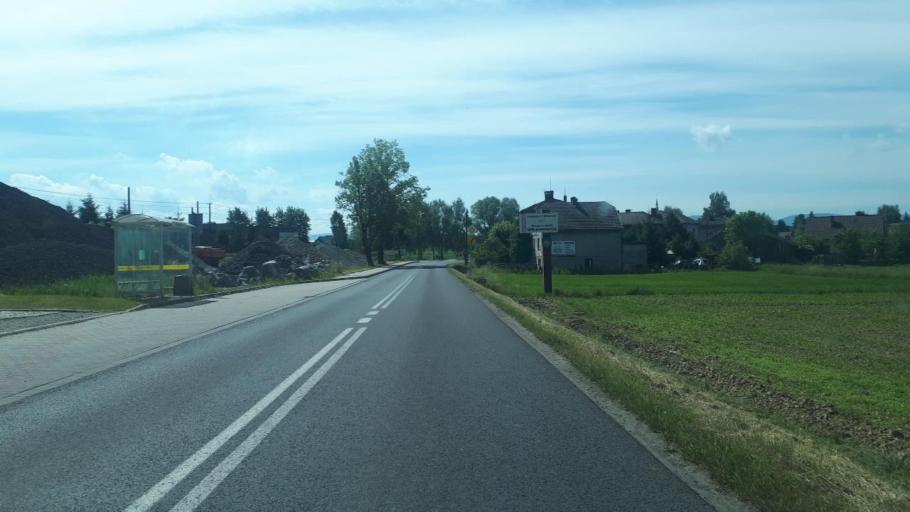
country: PL
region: Silesian Voivodeship
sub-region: Powiat bielski
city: Wilamowice
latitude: 49.9238
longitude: 19.1501
